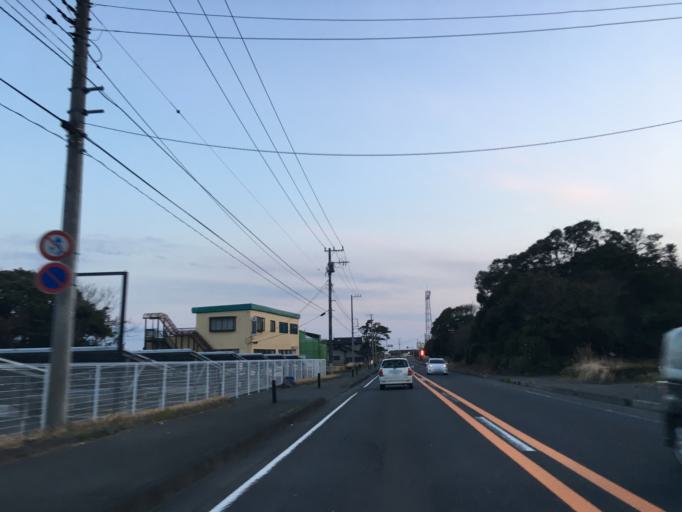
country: JP
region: Ibaraki
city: Kitaibaraki
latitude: 36.7624
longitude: 140.7371
